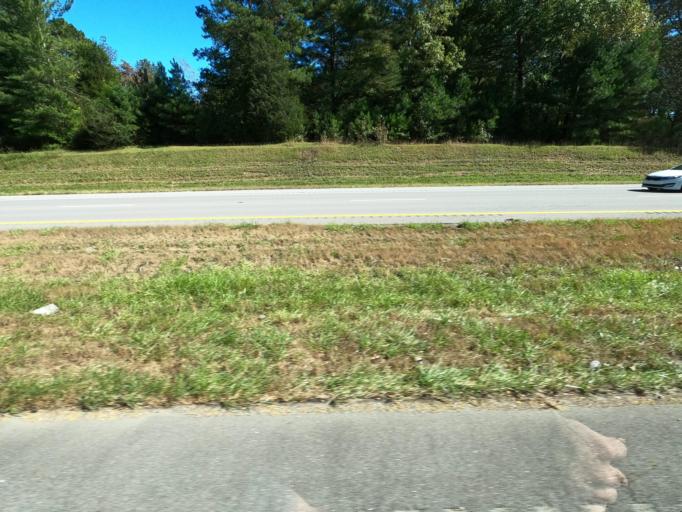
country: US
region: Tennessee
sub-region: Maury County
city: Mount Pleasant
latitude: 35.4214
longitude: -87.2823
